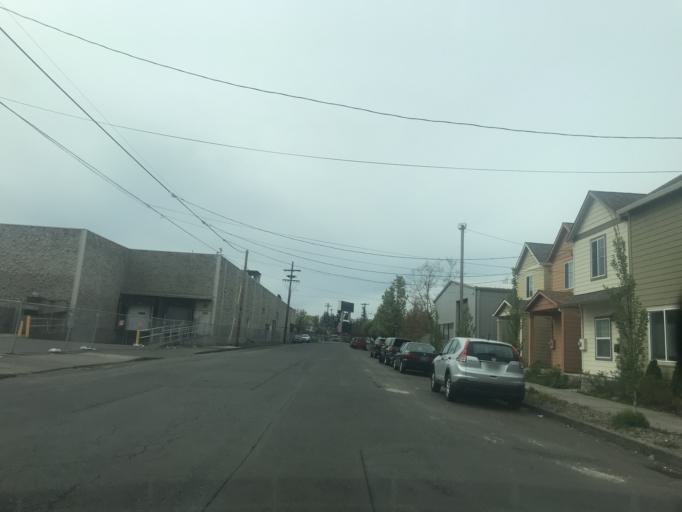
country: US
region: Oregon
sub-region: Multnomah County
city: Lents
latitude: 45.4852
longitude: -122.5808
